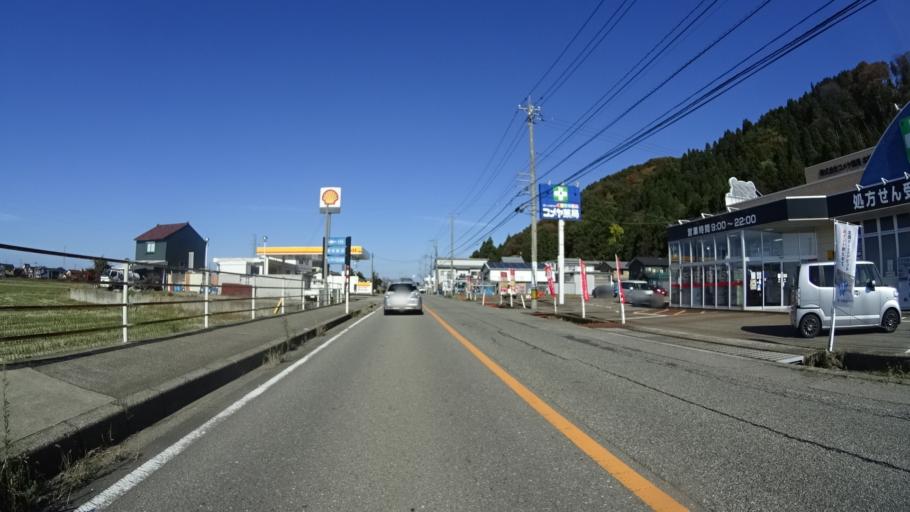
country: JP
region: Ishikawa
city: Tsurugi-asahimachi
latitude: 36.4660
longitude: 136.6192
